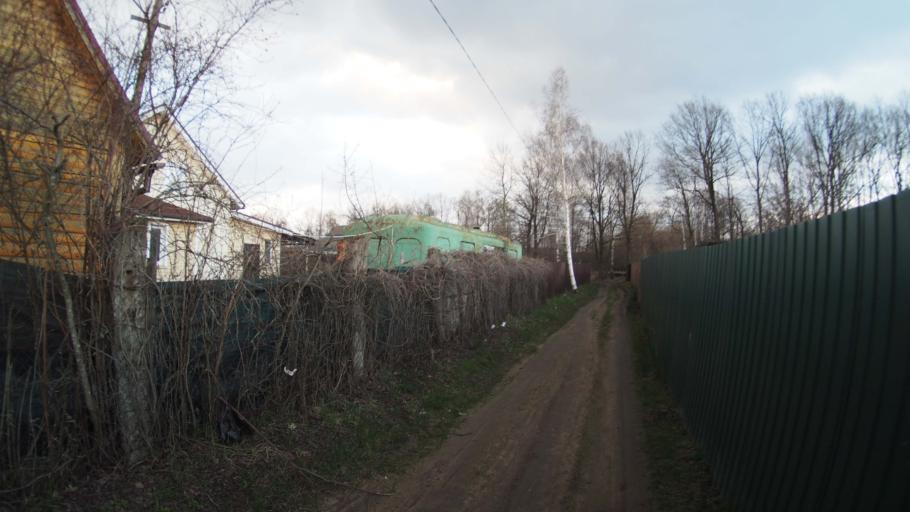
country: RU
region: Moskovskaya
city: Ramenskoye
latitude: 55.5390
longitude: 38.2967
